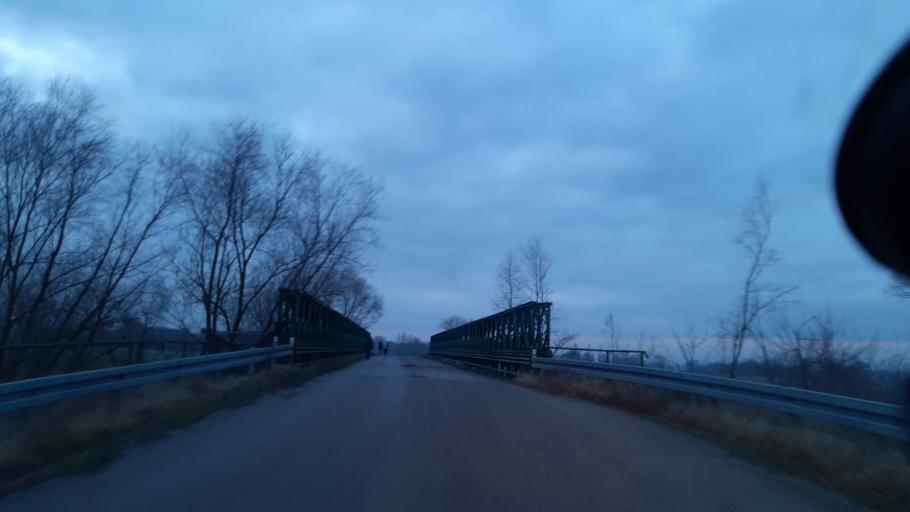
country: PL
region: Lublin Voivodeship
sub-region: Powiat lubartowski
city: Firlej
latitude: 51.5768
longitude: 22.5410
